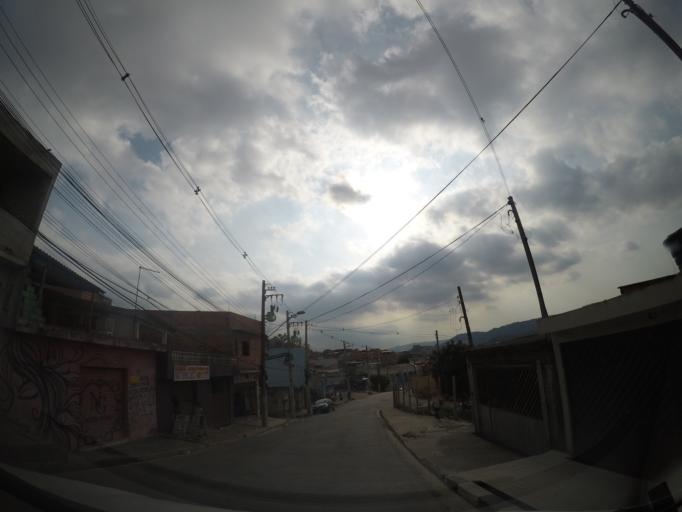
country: BR
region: Sao Paulo
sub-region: Guarulhos
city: Guarulhos
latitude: -23.4038
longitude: -46.5163
